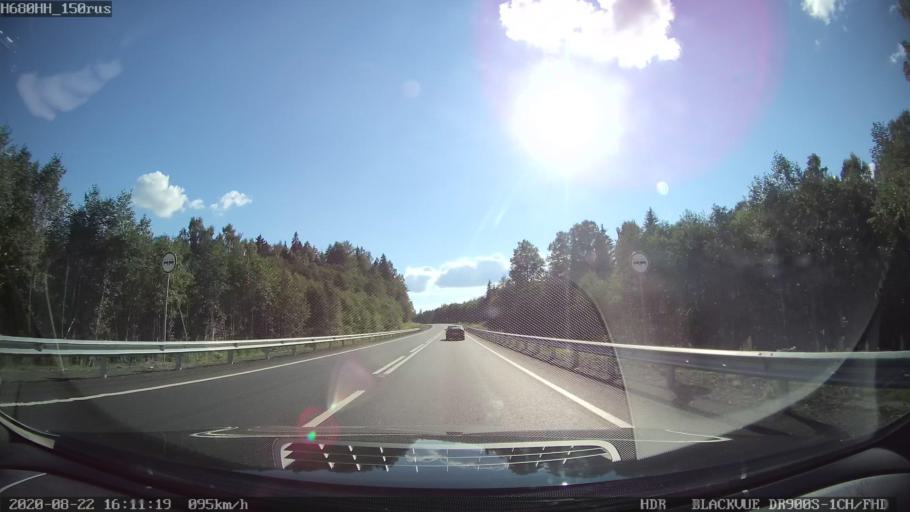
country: RU
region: Tverskaya
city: Rameshki
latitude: 57.5027
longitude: 36.2630
